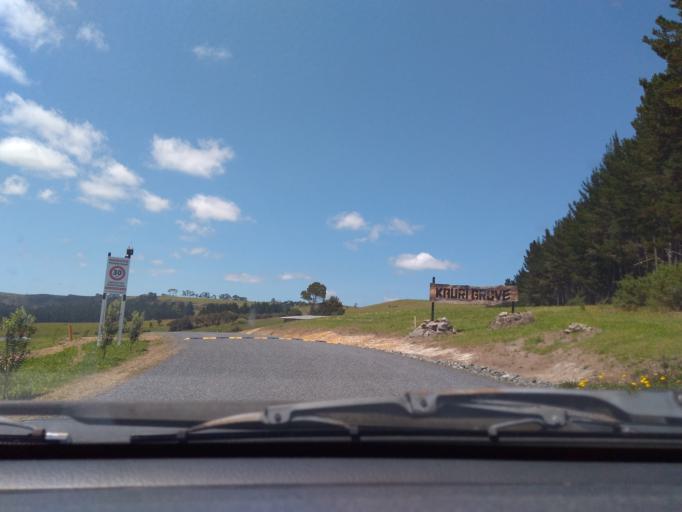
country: NZ
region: Northland
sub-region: Far North District
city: Taipa
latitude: -34.9957
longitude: 173.5112
